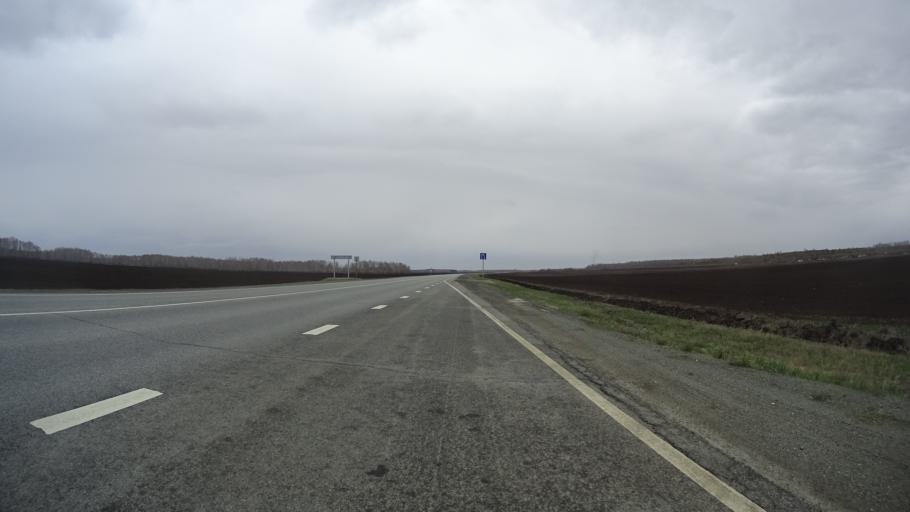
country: RU
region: Chelyabinsk
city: Krasnogorskiy
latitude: 54.5805
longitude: 61.2913
